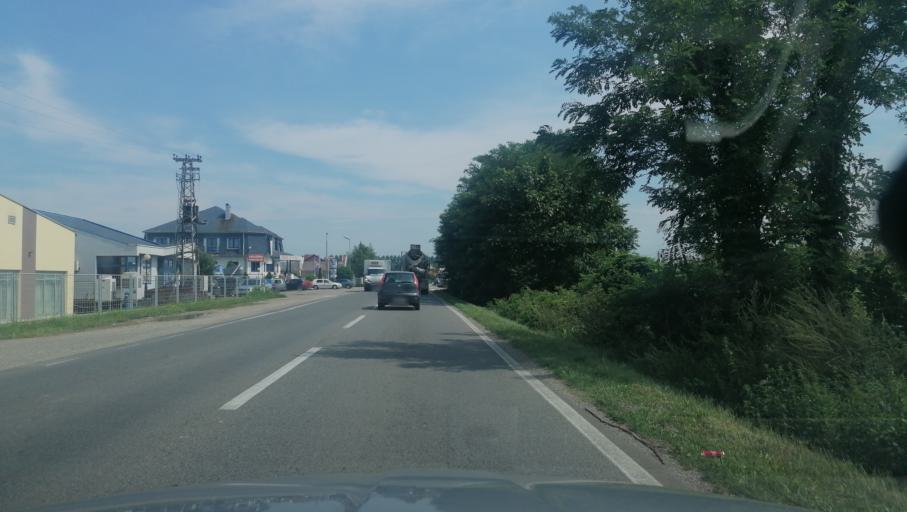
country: BA
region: Republika Srpska
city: Velika Obarska
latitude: 44.7680
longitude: 19.1639
